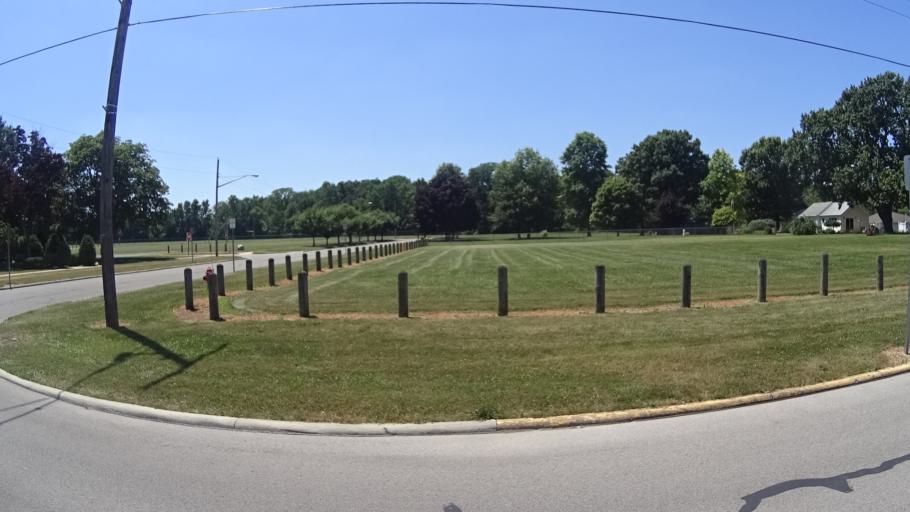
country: US
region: Ohio
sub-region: Erie County
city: Huron
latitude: 41.3983
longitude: -82.5646
